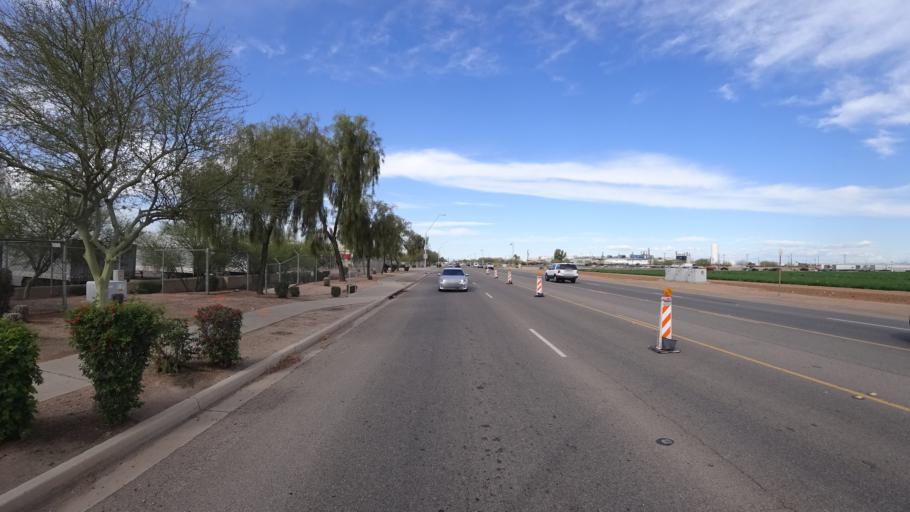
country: US
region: Arizona
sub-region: Maricopa County
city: Tolleson
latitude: 33.4378
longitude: -112.2553
